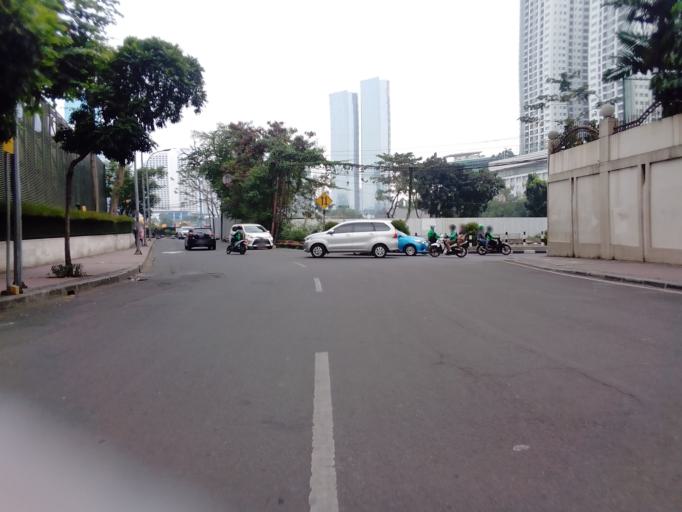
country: ID
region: Jakarta Raya
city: Jakarta
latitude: -6.1953
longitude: 106.8188
